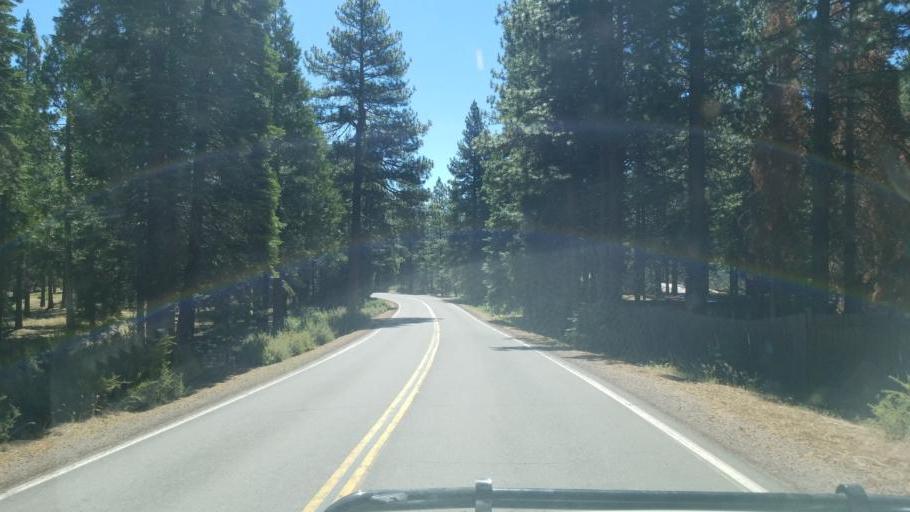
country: US
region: California
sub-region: Lassen County
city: Susanville
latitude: 40.4355
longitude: -120.7410
